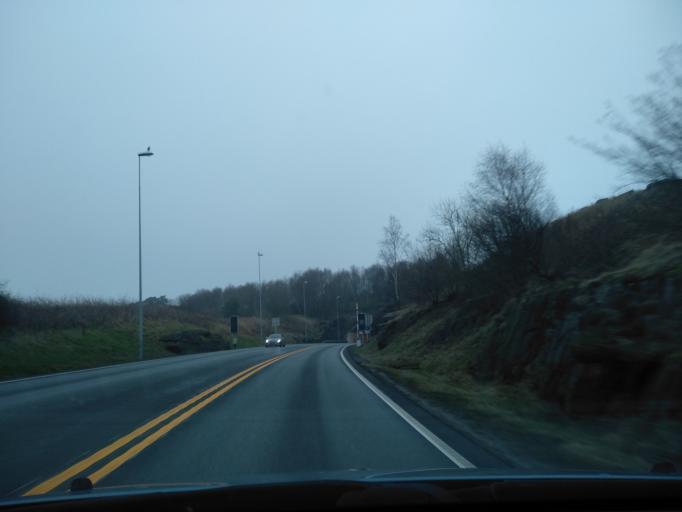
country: NO
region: Rogaland
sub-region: Rennesoy
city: Vikevag
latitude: 59.0710
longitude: 5.6750
